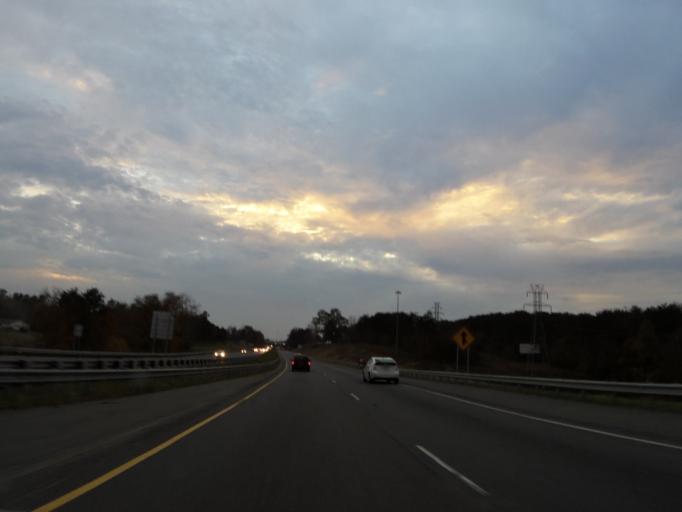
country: US
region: North Carolina
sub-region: Burke County
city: Morganton
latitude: 35.7222
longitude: -81.6572
